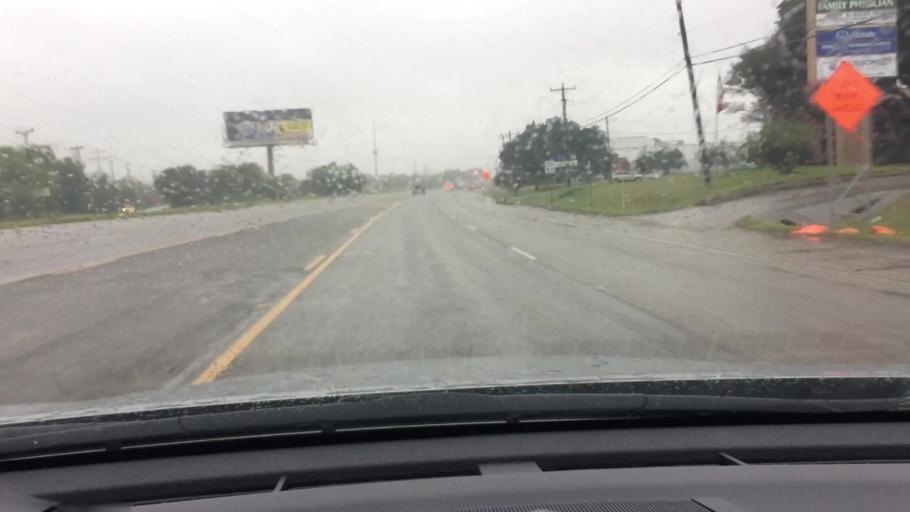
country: US
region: Texas
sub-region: Bexar County
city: Kirby
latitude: 29.4757
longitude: -98.3721
